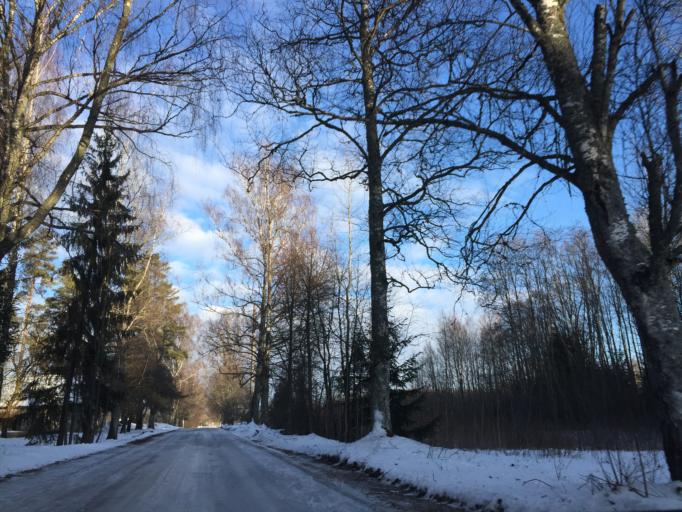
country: LV
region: Kegums
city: Kegums
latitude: 56.7397
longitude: 24.6657
